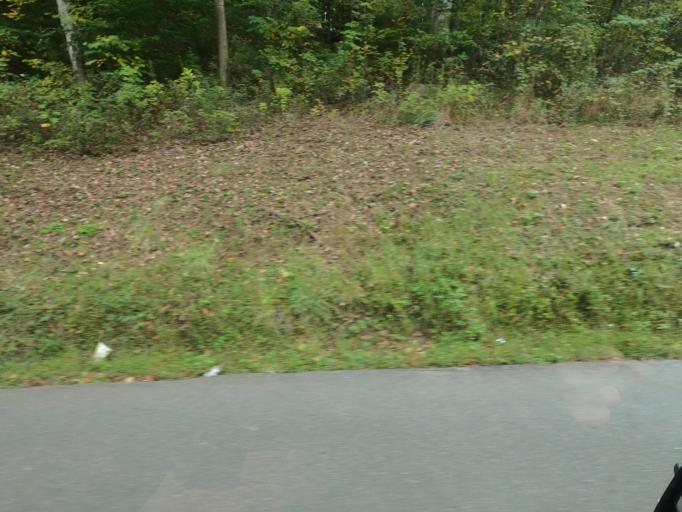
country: US
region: Tennessee
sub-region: Washington County
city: Jonesborough
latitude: 36.2694
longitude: -82.5345
